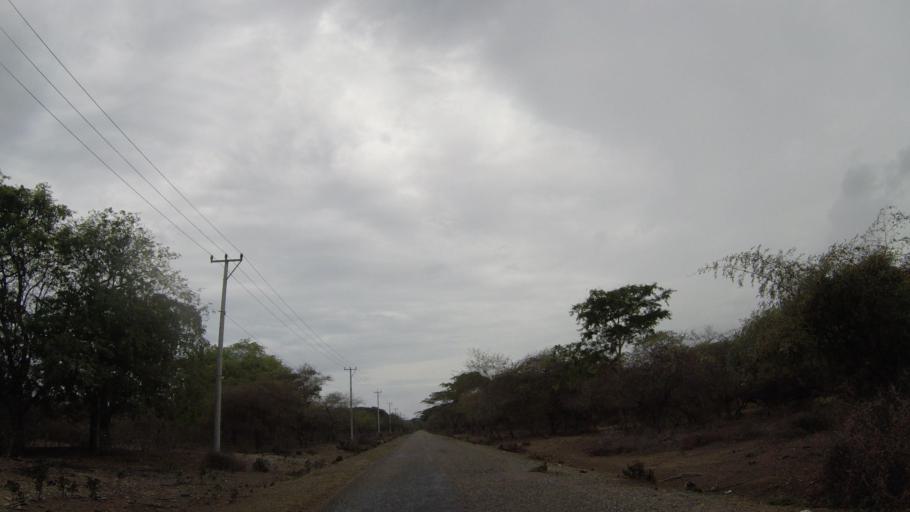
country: TL
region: Lautem
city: Lospalos
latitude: -8.3266
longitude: 126.9889
